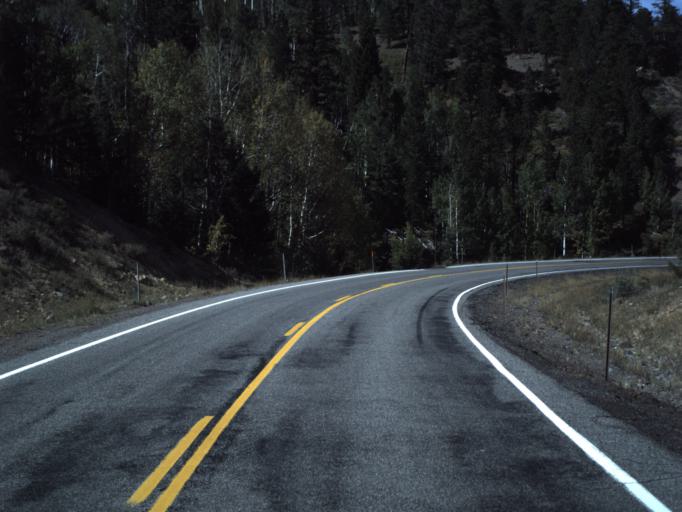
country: US
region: Utah
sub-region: Wayne County
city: Loa
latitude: 38.1493
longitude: -111.3318
